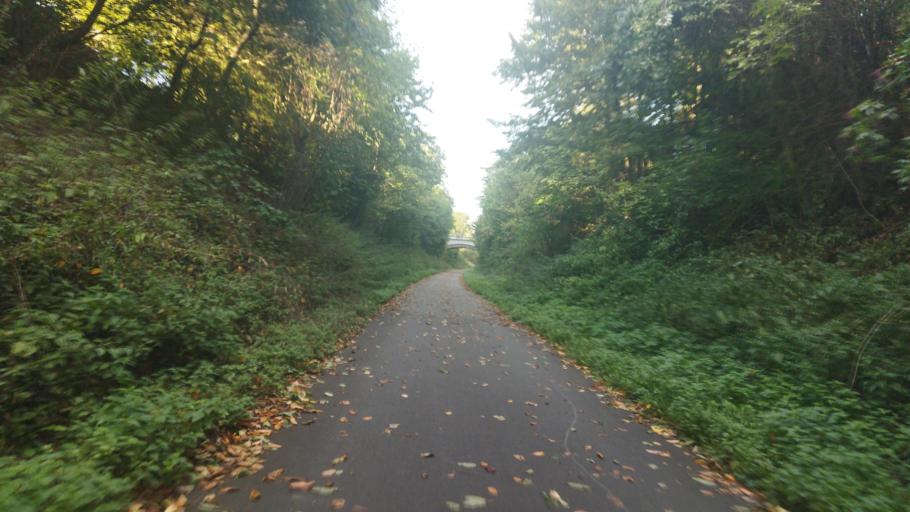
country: DE
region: North Rhine-Westphalia
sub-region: Regierungsbezirk Munster
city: Billerbeck
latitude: 51.9940
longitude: 7.2383
